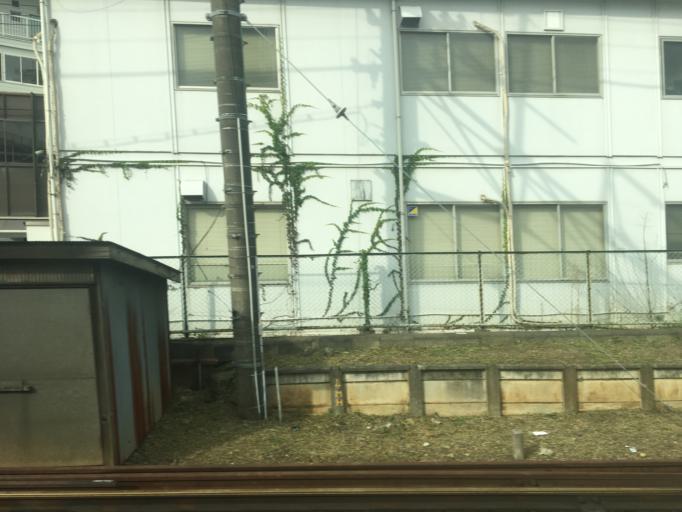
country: JP
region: Saitama
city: Sayama
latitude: 35.8561
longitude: 139.4130
